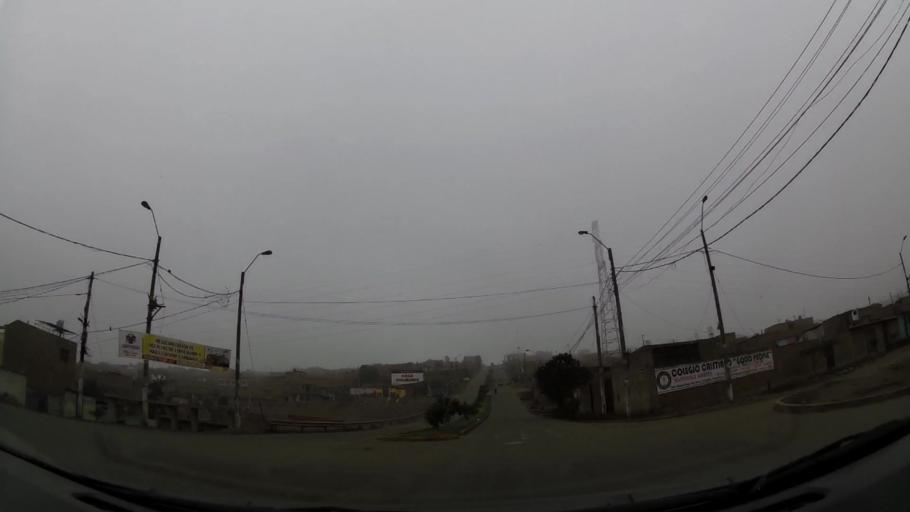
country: PE
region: Lima
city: Ventanilla
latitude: -11.8338
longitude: -77.1078
